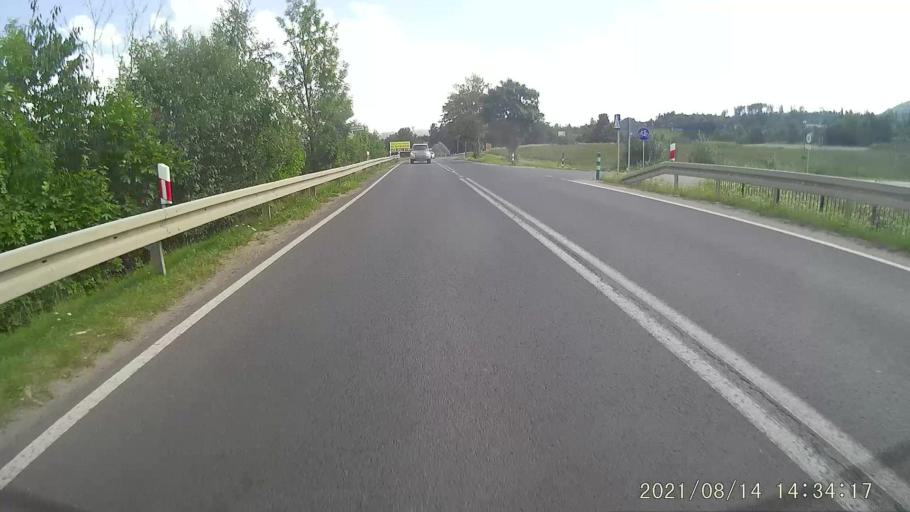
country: PL
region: Lower Silesian Voivodeship
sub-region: Powiat klodzki
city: Nowa Ruda
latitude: 50.5645
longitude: 16.5353
